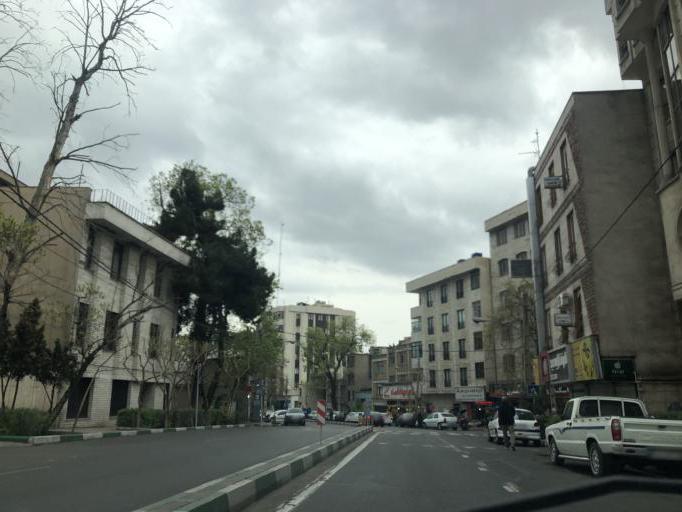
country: IR
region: Tehran
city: Tajrish
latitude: 35.7763
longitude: 51.4396
